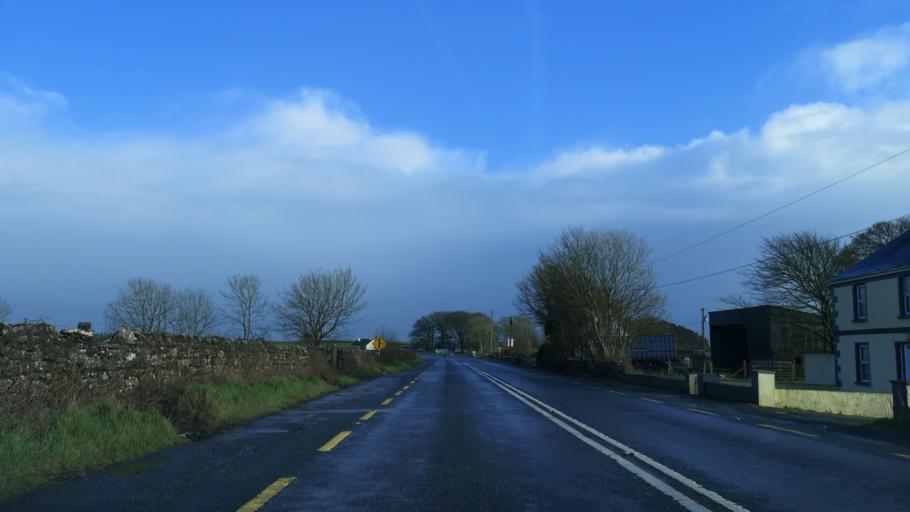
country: IE
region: Connaught
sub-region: County Galway
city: Tuam
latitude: 53.4924
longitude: -8.9004
